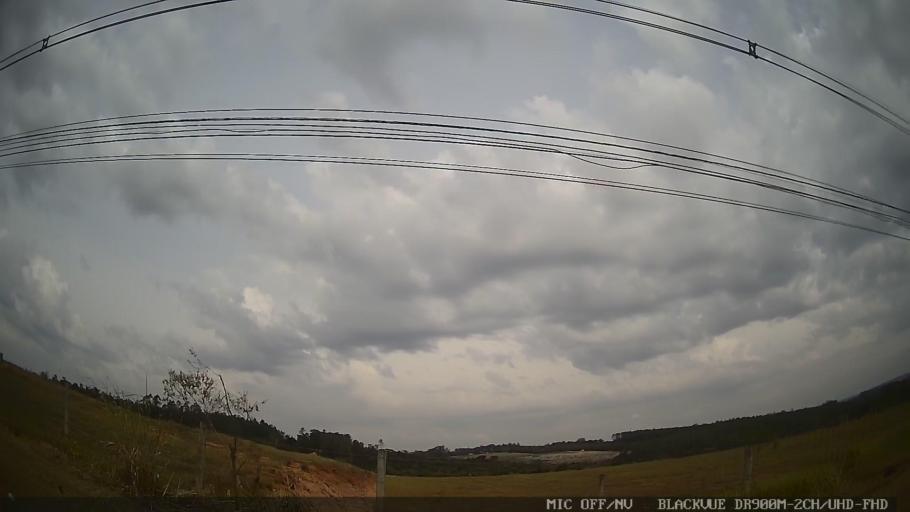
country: BR
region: Sao Paulo
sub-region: Indaiatuba
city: Indaiatuba
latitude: -23.1274
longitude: -47.2585
